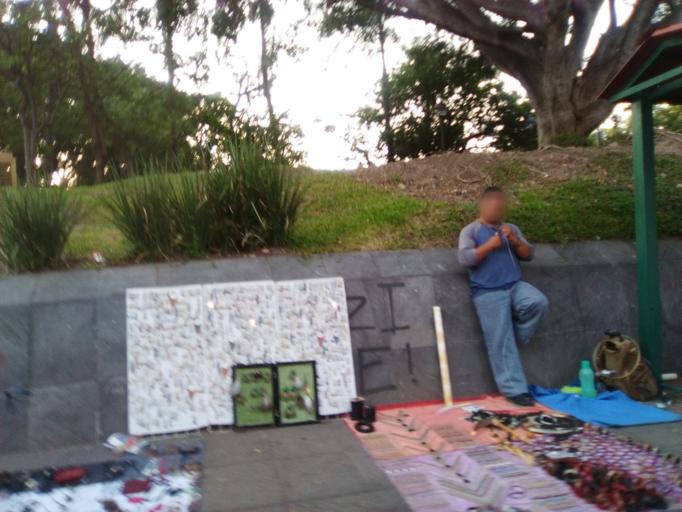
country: MX
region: Morelos
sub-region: Cuernavaca
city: Cuernavaca
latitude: 18.9216
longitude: -99.2337
